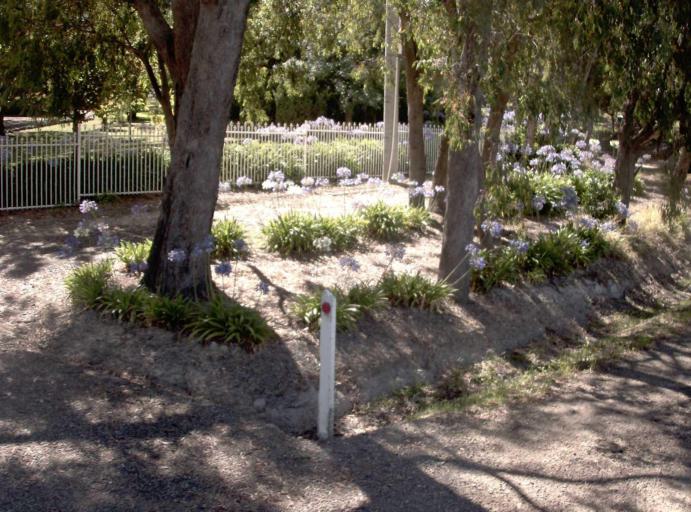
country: AU
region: Victoria
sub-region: Yarra Ranges
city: Healesville
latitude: -37.6737
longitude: 145.5397
